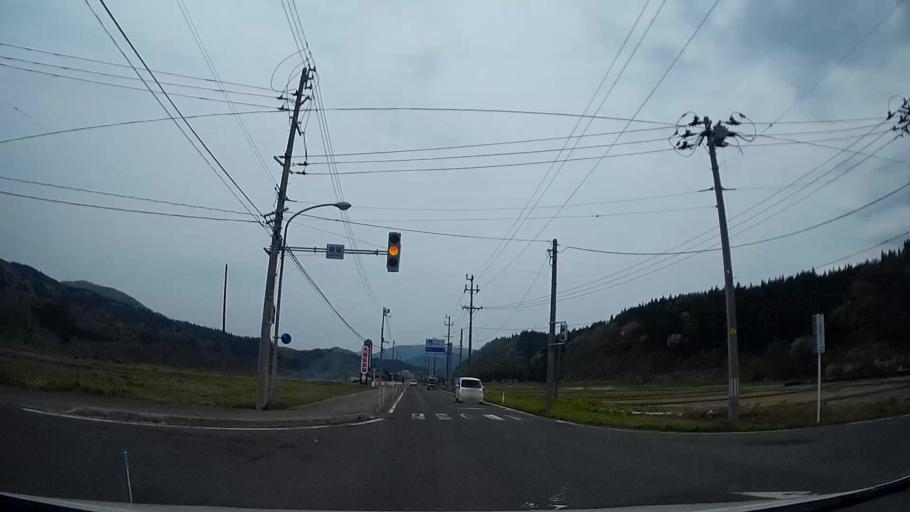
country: JP
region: Akita
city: Hanawa
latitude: 40.2875
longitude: 140.8083
